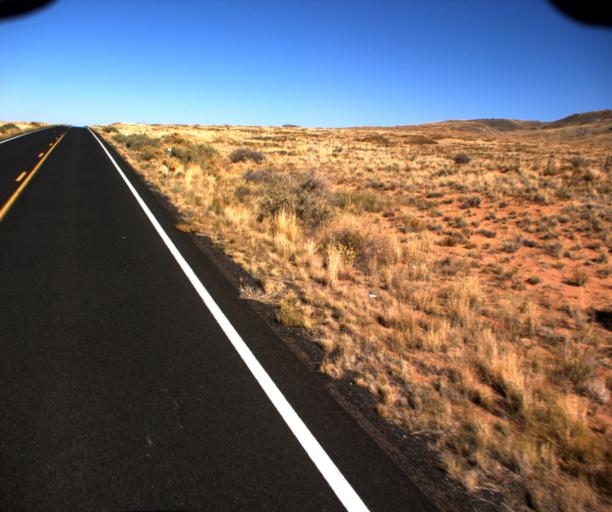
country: US
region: Arizona
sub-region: Navajo County
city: Dilkon
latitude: 35.4112
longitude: -110.4265
